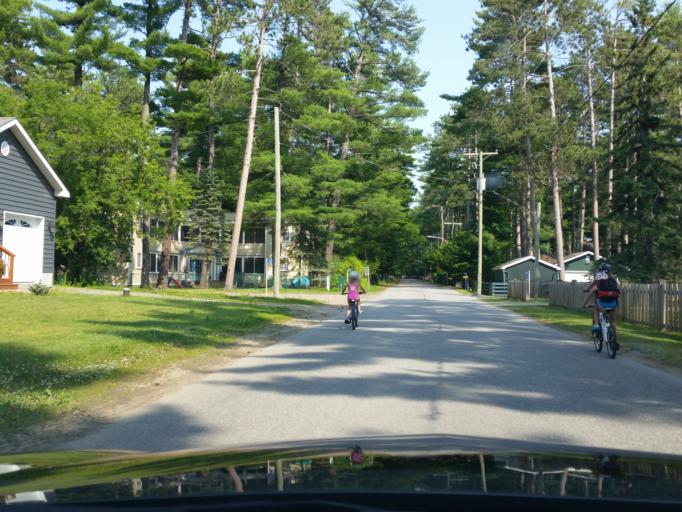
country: CA
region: Quebec
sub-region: Outaouais
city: Shawville
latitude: 45.5175
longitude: -76.4184
